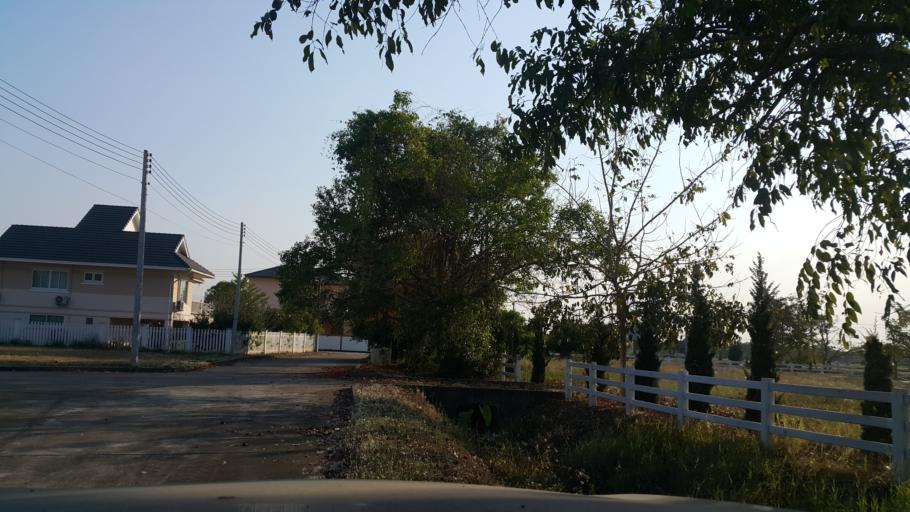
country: TH
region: Chiang Mai
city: San Sai
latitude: 18.8390
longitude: 99.0981
